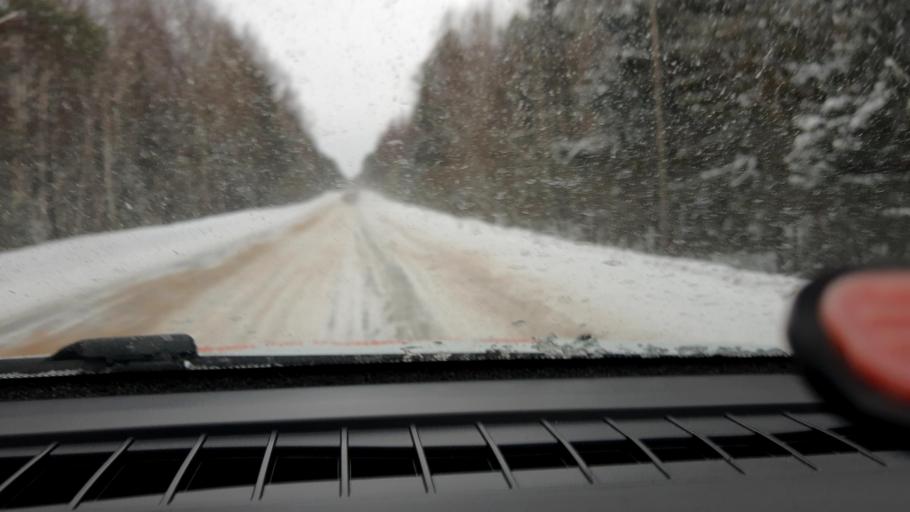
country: RU
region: Nizjnij Novgorod
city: Pamyat' Parizhskoy Kommuny
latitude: 56.2603
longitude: 44.4505
